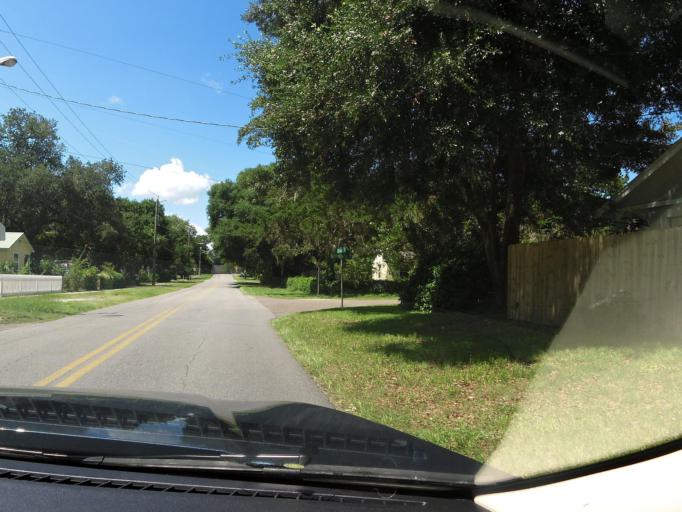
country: US
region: Florida
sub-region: Nassau County
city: Fernandina Beach
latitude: 30.6669
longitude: -81.4437
